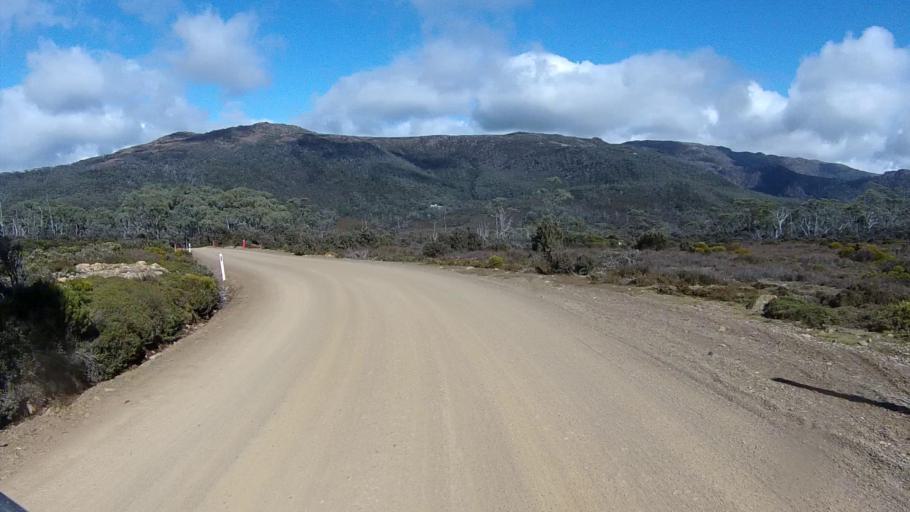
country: AU
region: Tasmania
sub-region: Derwent Valley
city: New Norfolk
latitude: -42.6824
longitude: 146.6085
